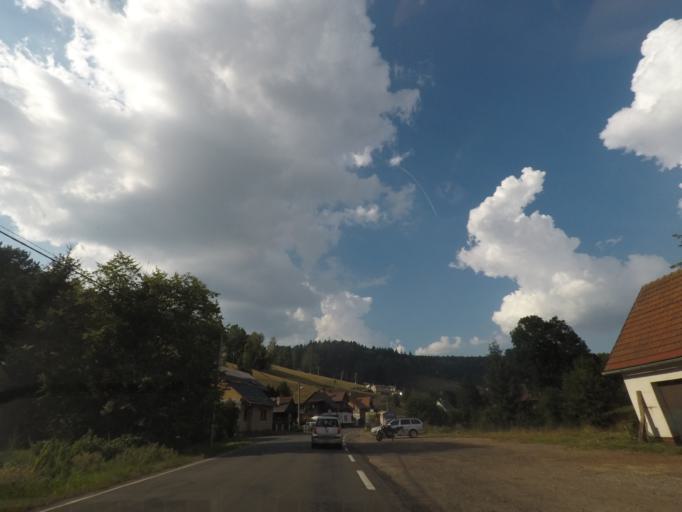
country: CZ
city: Velke Svatonovice
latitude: 50.5950
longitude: 15.9904
